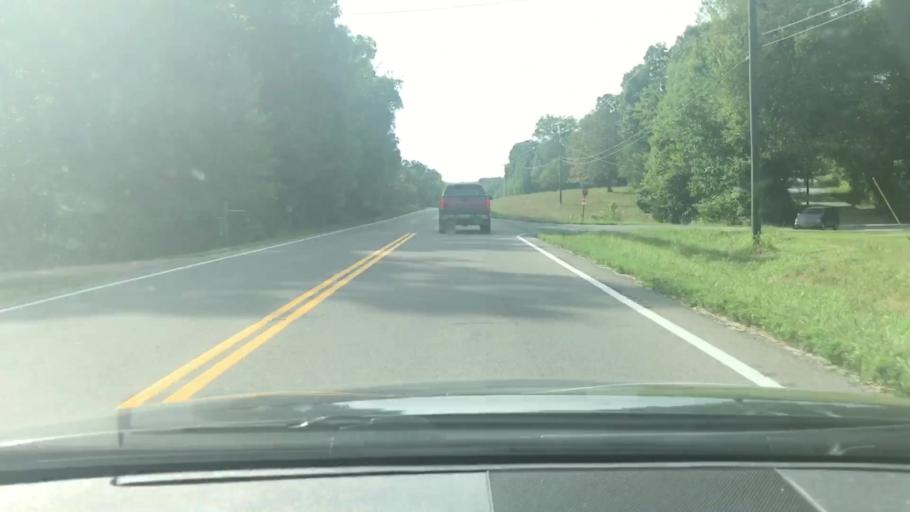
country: US
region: Tennessee
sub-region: Williamson County
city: Fairview
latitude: 36.0109
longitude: -87.1476
